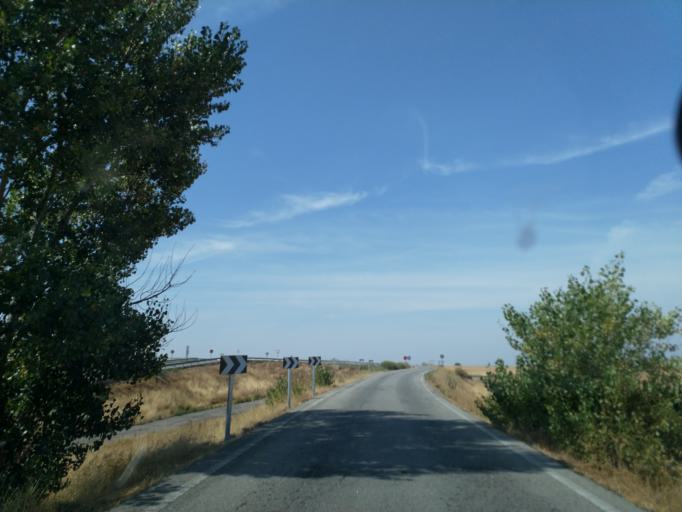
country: ES
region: Extremadura
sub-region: Provincia de Caceres
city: Berrocalejo
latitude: 39.8955
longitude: -5.3438
